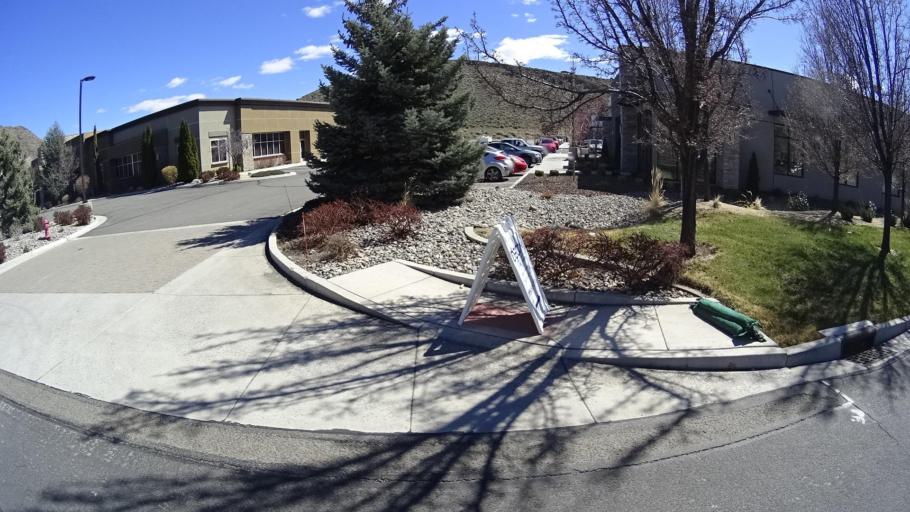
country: US
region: Nevada
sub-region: Washoe County
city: Sparks
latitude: 39.4677
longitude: -119.7646
